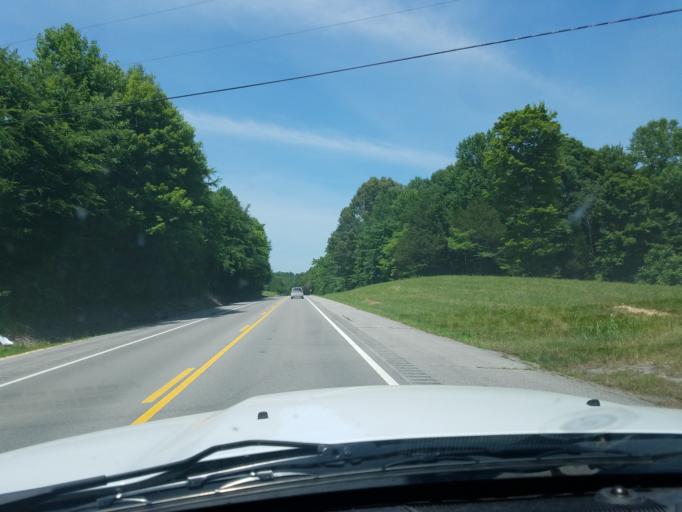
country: US
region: Tennessee
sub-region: Sumner County
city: Westmoreland
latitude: 36.5988
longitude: -86.2334
